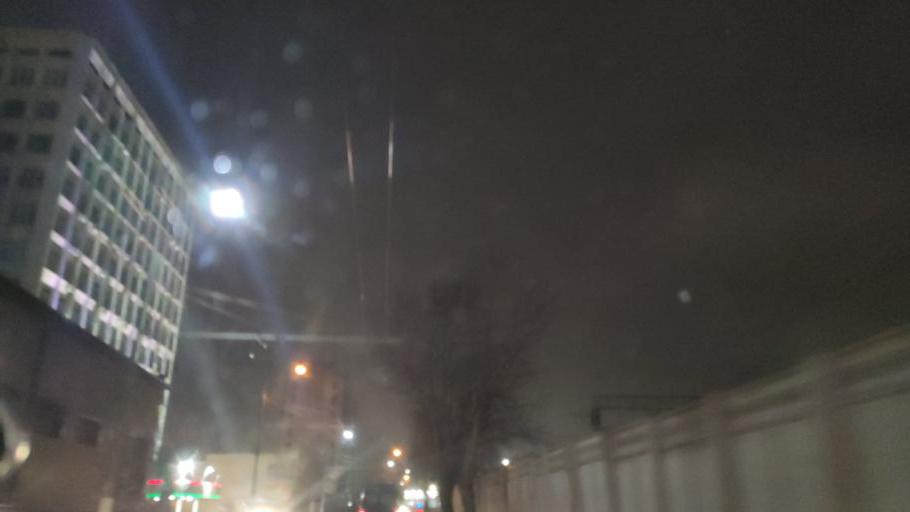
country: RU
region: Moskovskaya
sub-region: Podol'skiy Rayon
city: Podol'sk
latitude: 55.4302
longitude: 37.5657
